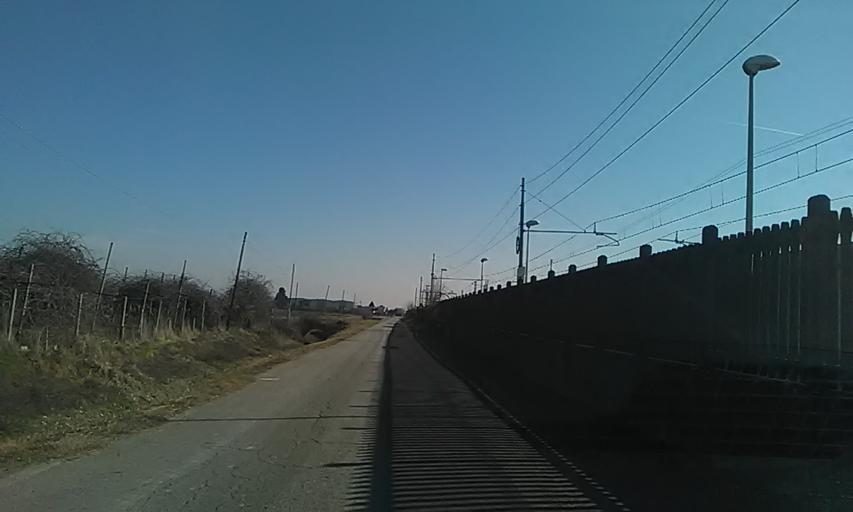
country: IT
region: Piedmont
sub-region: Provincia di Vercelli
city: San Germano Vercellese
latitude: 45.3537
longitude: 8.2498
